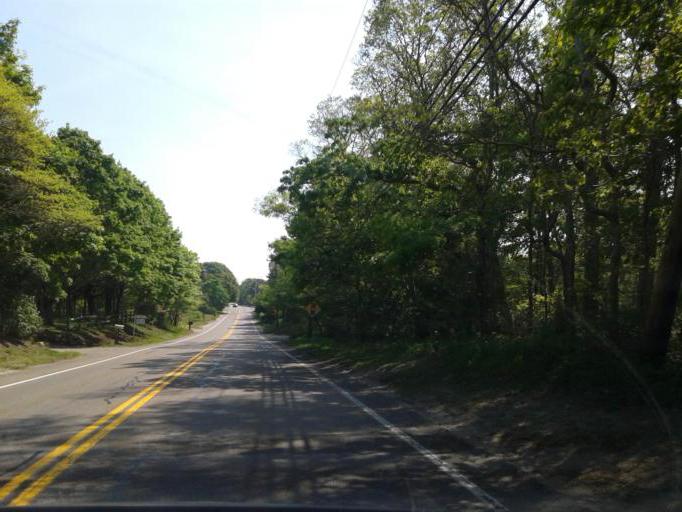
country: US
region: Massachusetts
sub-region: Barnstable County
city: Teaticket
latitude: 41.5857
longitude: -70.5864
